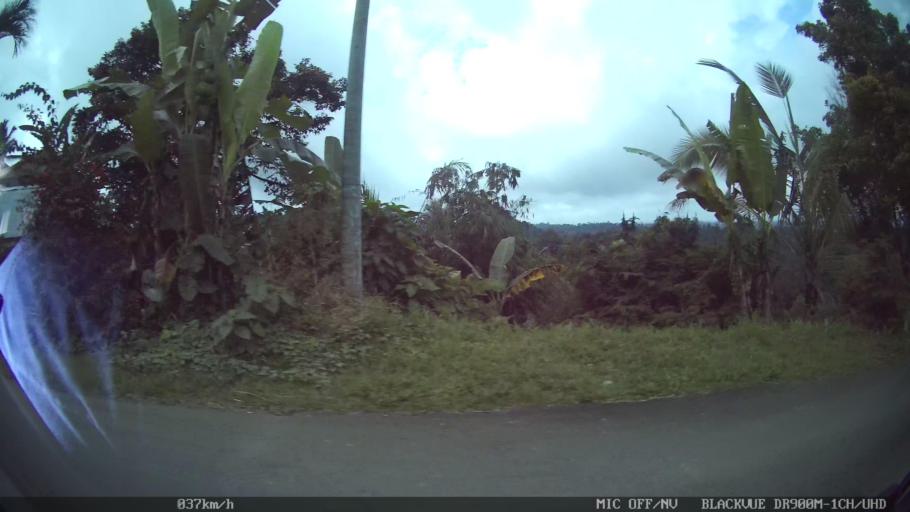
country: ID
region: Bali
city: Peneng
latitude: -8.3551
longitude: 115.2094
